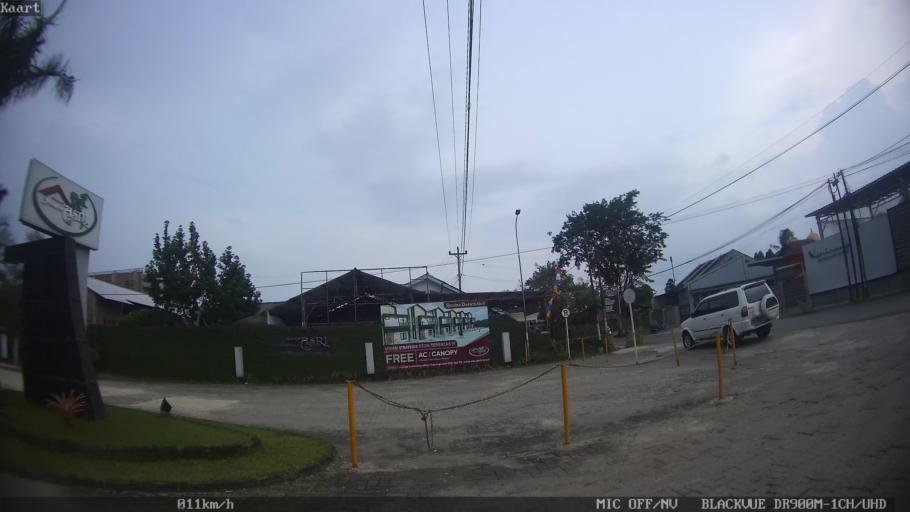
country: ID
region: Lampung
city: Bandarlampung
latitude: -5.4135
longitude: 105.2850
